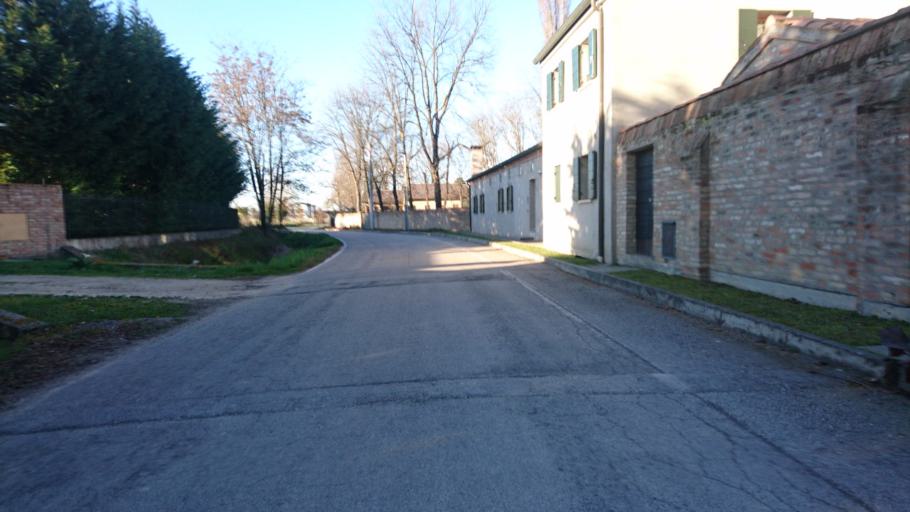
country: IT
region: Veneto
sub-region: Provincia di Padova
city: Bertipaglia
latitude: 45.3042
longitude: 11.8847
